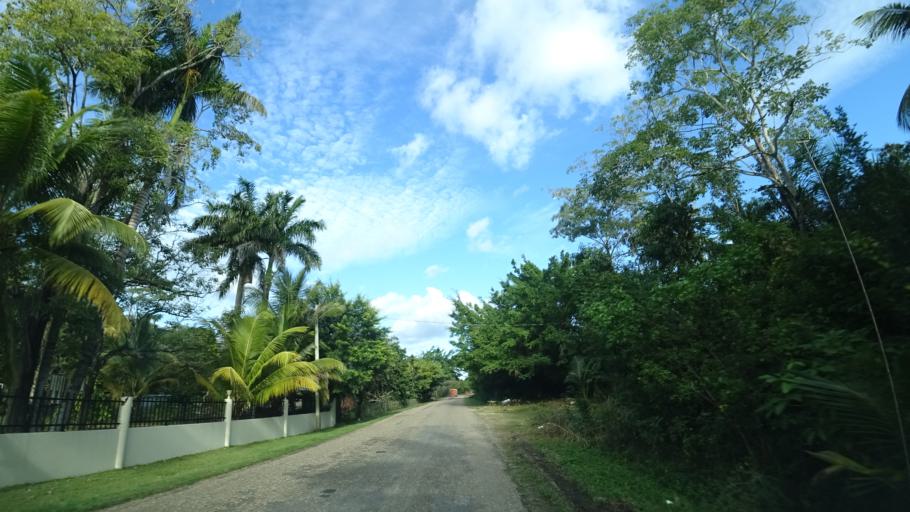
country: BZ
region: Belize
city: Belize City
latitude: 17.5707
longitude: -88.3957
